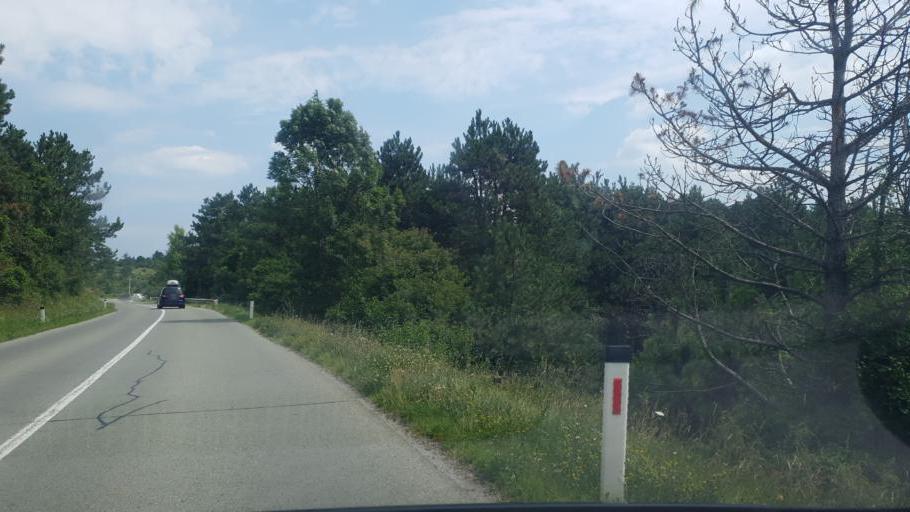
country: SI
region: Ilirska Bistrica
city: Ilirska Bistrica
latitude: 45.6129
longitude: 14.2490
